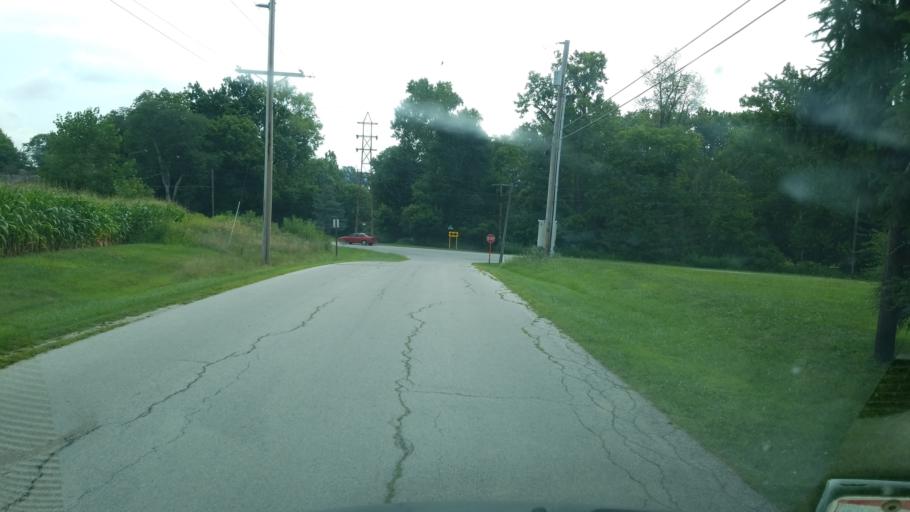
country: US
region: Ohio
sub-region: Sandusky County
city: Ballville
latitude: 41.2987
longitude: -83.1649
